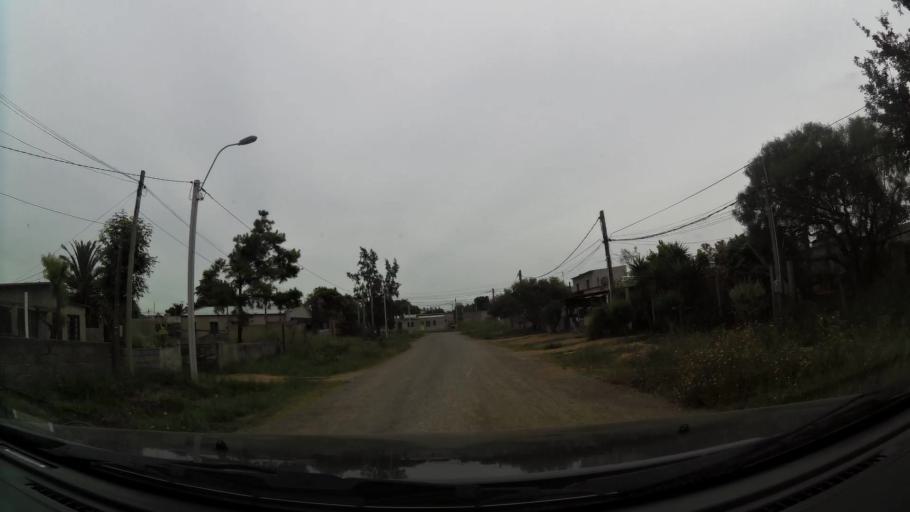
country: UY
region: Canelones
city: Las Piedras
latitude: -34.7315
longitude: -56.2046
